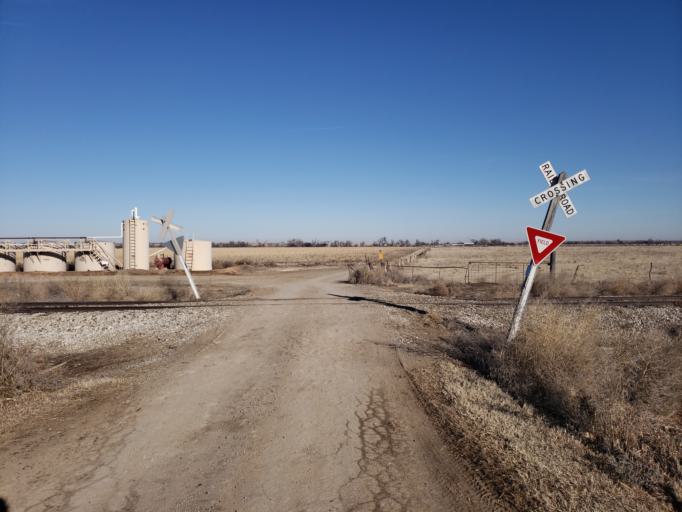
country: US
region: Kansas
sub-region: Rush County
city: La Crosse
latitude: 38.4626
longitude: -99.5950
